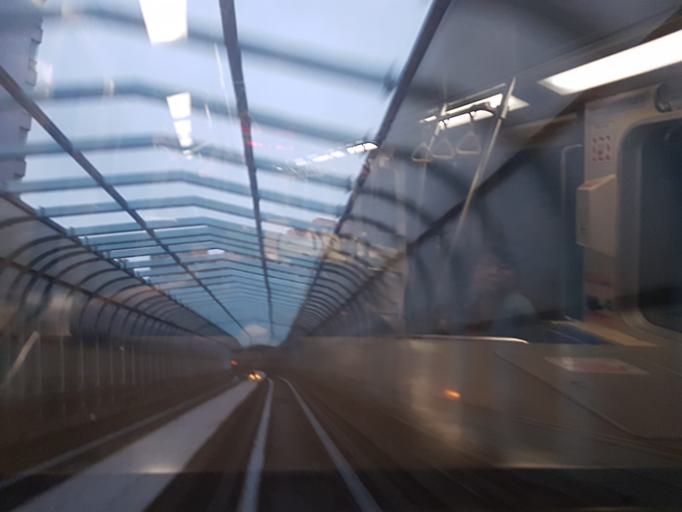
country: TW
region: Taipei
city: Taipei
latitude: 25.0742
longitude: 121.6065
